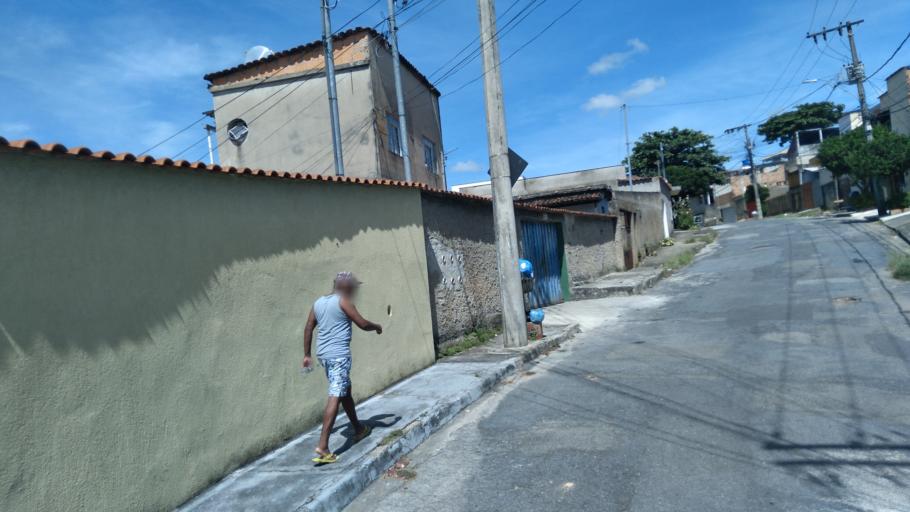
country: BR
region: Minas Gerais
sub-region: Contagem
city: Contagem
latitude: -19.8941
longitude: -44.0124
